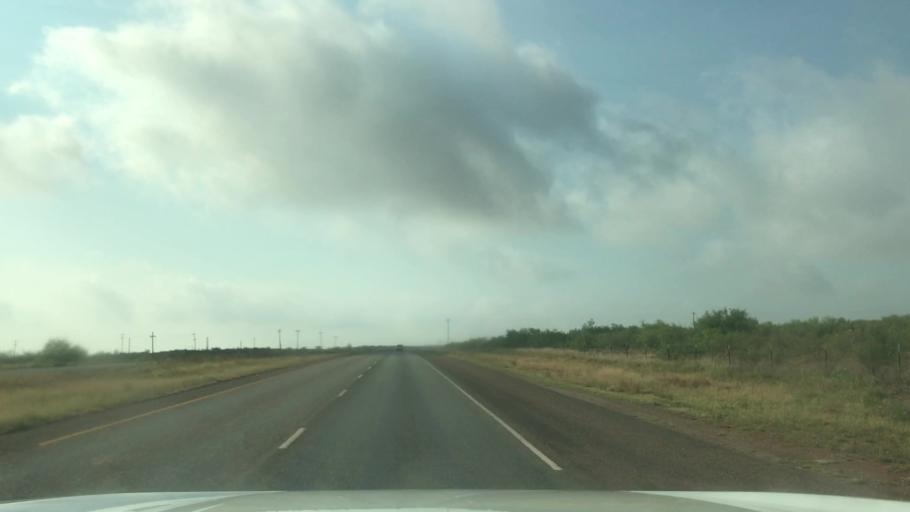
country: US
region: Texas
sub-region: Garza County
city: Post
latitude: 33.1649
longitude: -101.3503
